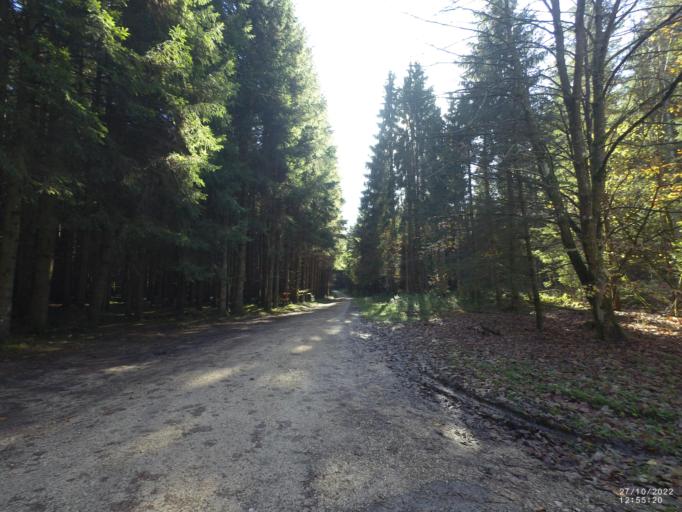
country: DE
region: Baden-Wuerttemberg
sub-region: Regierungsbezirk Stuttgart
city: Bohmenkirch
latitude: 48.7261
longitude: 9.9416
